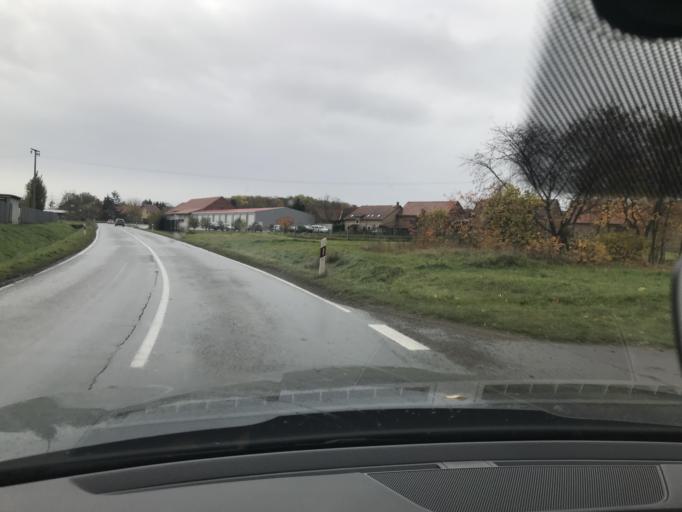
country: DE
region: Saxony-Anhalt
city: Harsleben
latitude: 51.8704
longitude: 11.1072
